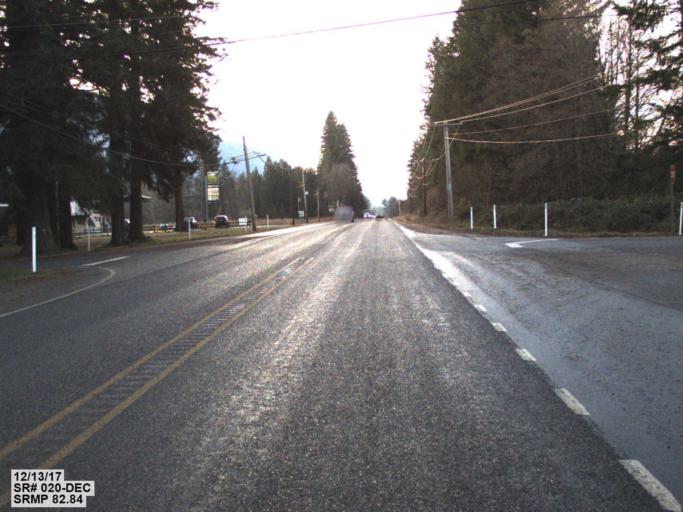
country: US
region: Washington
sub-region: Skagit County
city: Sedro-Woolley
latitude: 48.5345
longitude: -121.8759
